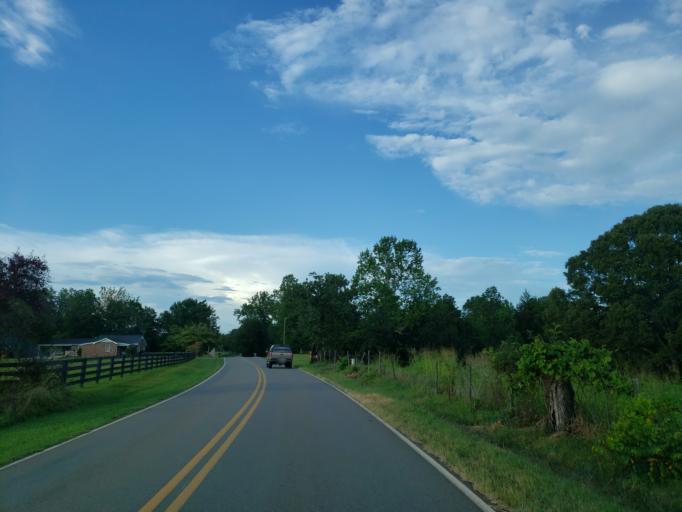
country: US
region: Georgia
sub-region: Cherokee County
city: Ball Ground
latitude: 34.3308
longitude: -84.4570
